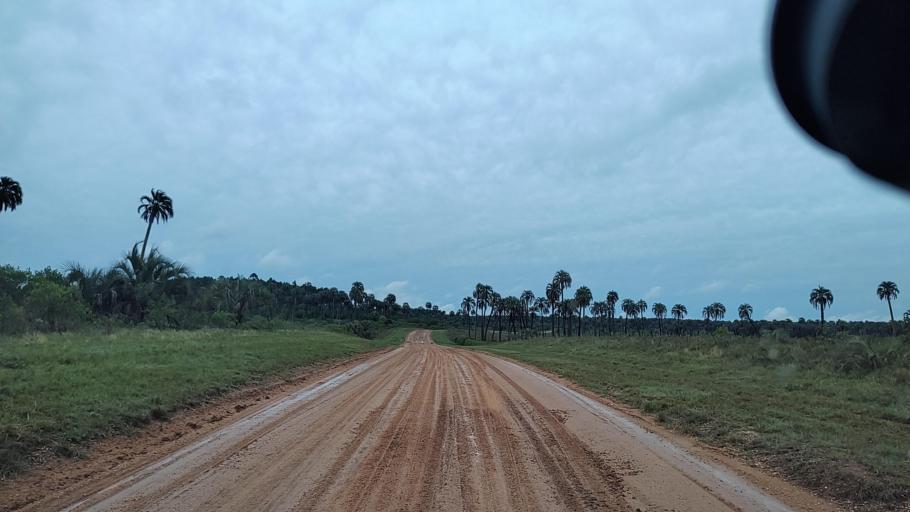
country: AR
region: Entre Rios
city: Ubajay
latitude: -31.8511
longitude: -58.3118
